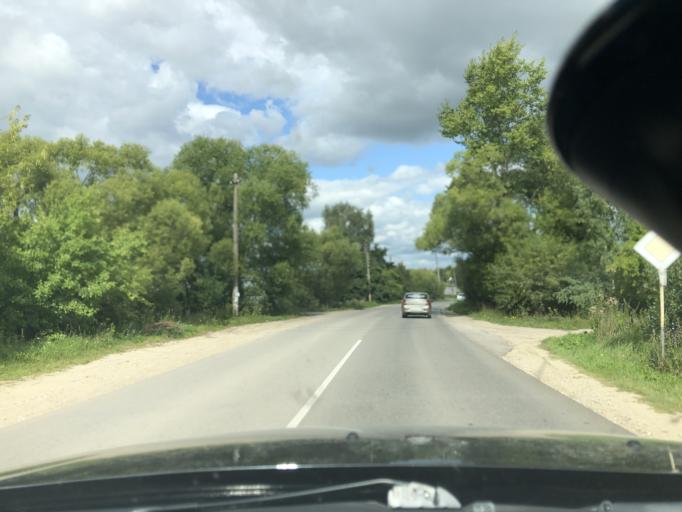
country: RU
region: Tula
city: Yasnogorsk
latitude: 54.4647
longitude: 37.7036
